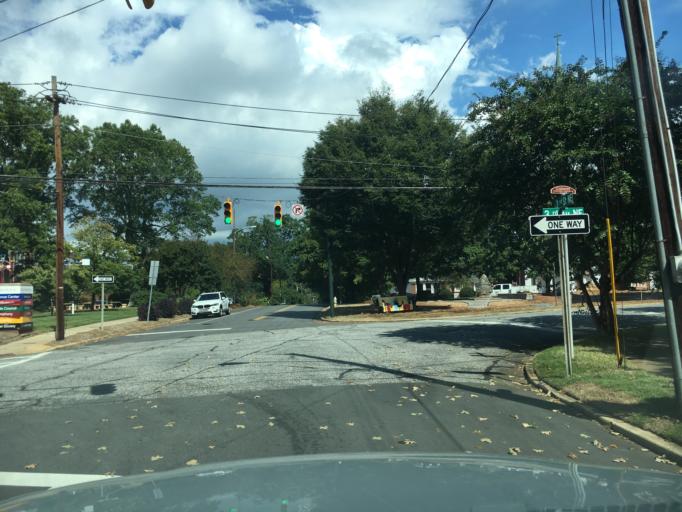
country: US
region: North Carolina
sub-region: Catawba County
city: Hickory
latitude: 35.7354
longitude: -81.3331
